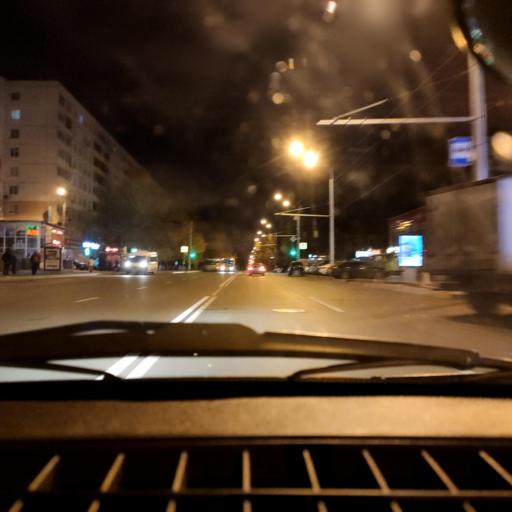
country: RU
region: Bashkortostan
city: Ufa
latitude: 54.6961
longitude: 55.9968
